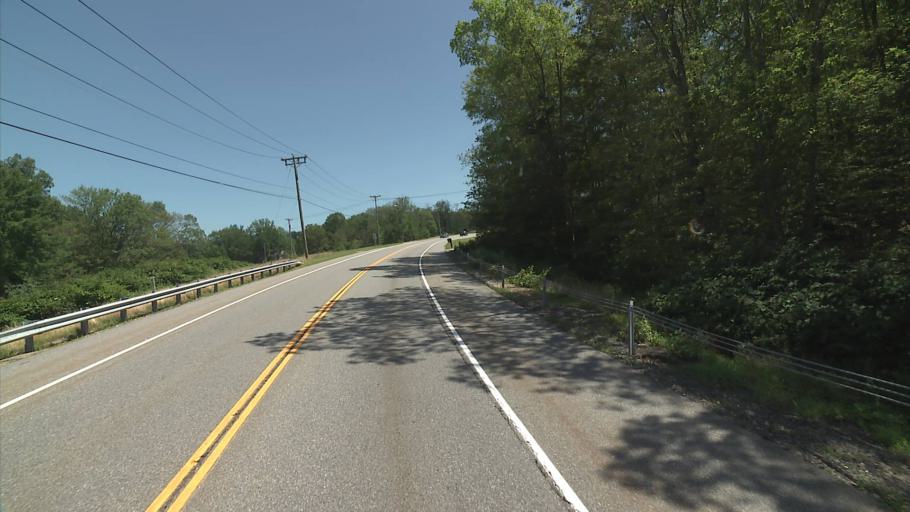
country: US
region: Connecticut
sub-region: Windham County
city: Moosup
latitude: 41.6862
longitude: -71.8577
